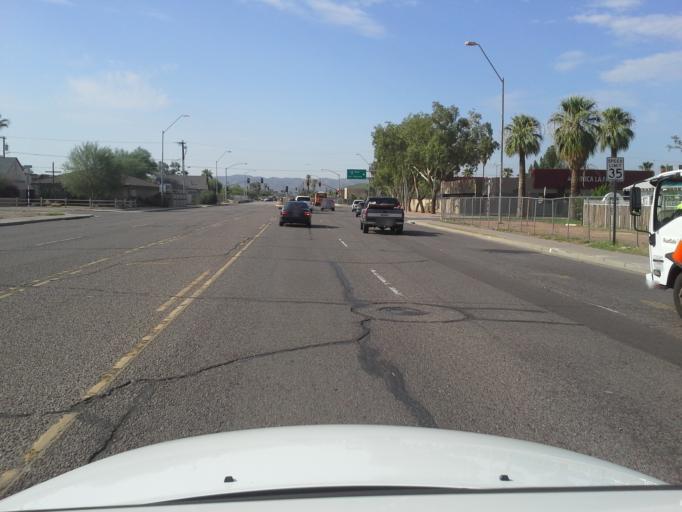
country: US
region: Arizona
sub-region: Maricopa County
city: Phoenix
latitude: 33.4643
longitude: -112.0477
